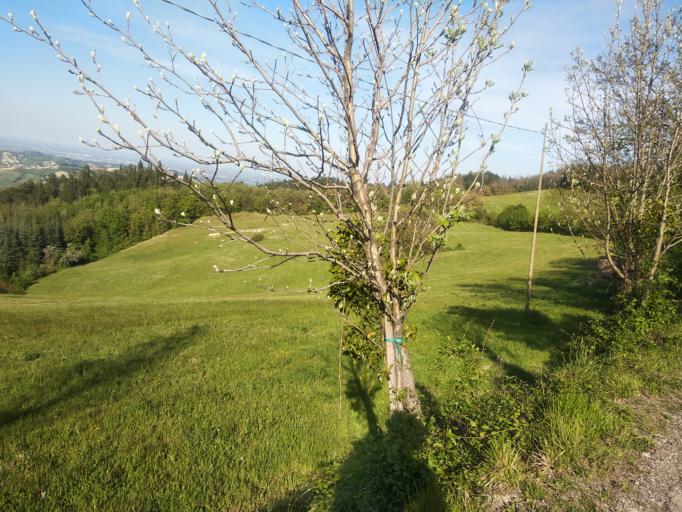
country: IT
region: Emilia-Romagna
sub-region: Provincia di Ravenna
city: Fognano
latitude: 44.2235
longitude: 11.7356
